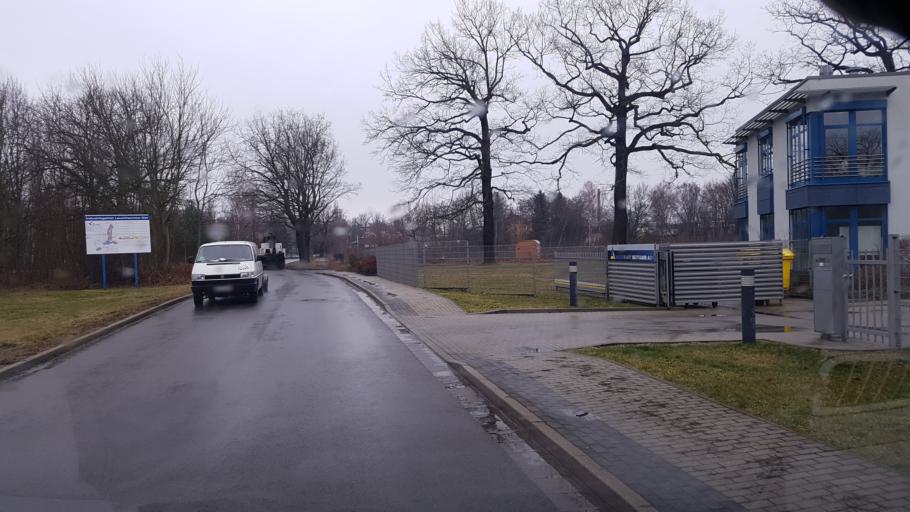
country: DE
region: Brandenburg
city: Lauchhammer
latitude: 51.4991
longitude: 13.8020
